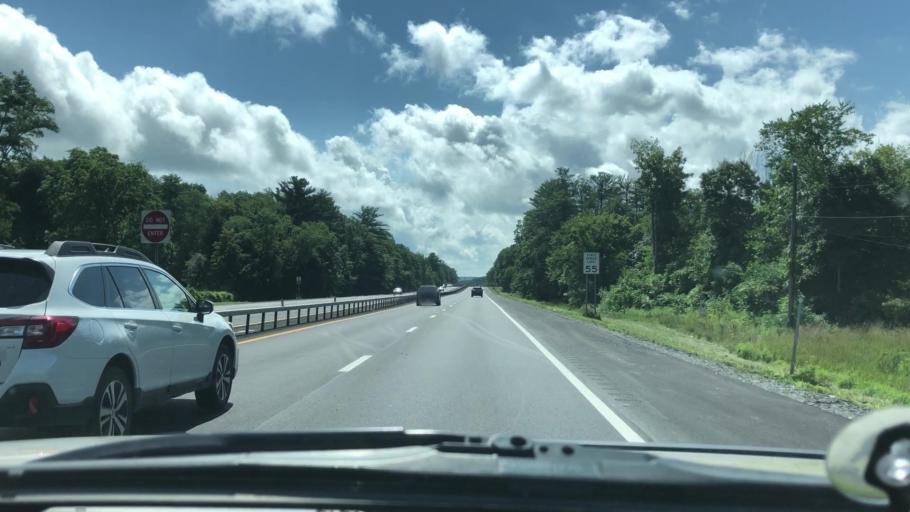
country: US
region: New York
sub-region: Greene County
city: Cairo
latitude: 42.3005
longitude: -73.9936
